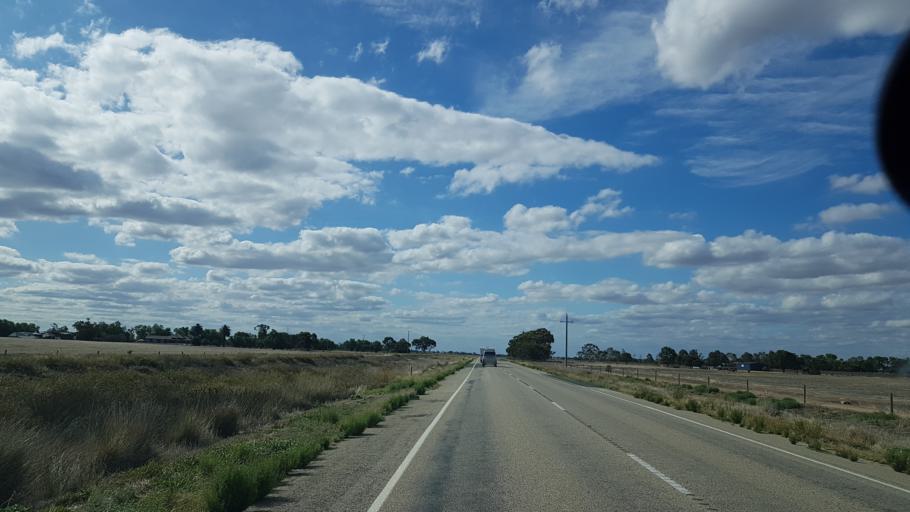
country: AU
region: Victoria
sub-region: Swan Hill
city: Swan Hill
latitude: -35.8060
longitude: 143.9557
